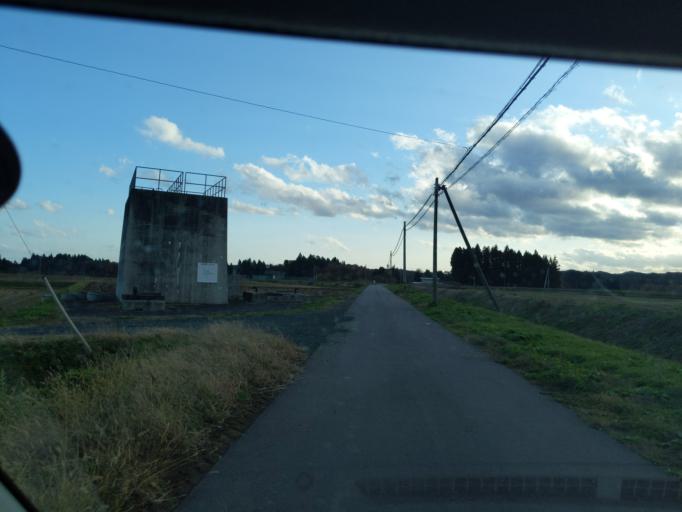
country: JP
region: Iwate
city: Mizusawa
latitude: 39.0898
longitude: 141.0370
